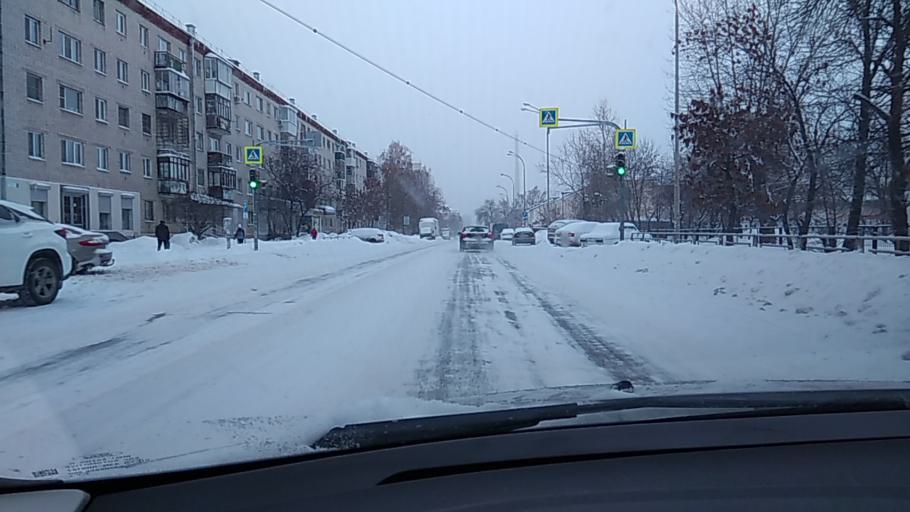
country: RU
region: Sverdlovsk
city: Yekaterinburg
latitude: 56.8105
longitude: 60.6125
